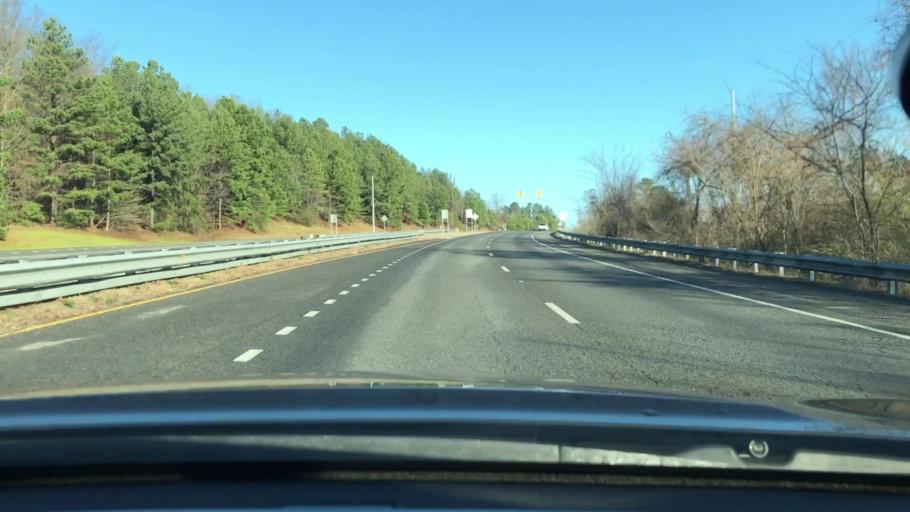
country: US
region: Alabama
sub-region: Shelby County
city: Meadowbrook
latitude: 33.3844
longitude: -86.6682
